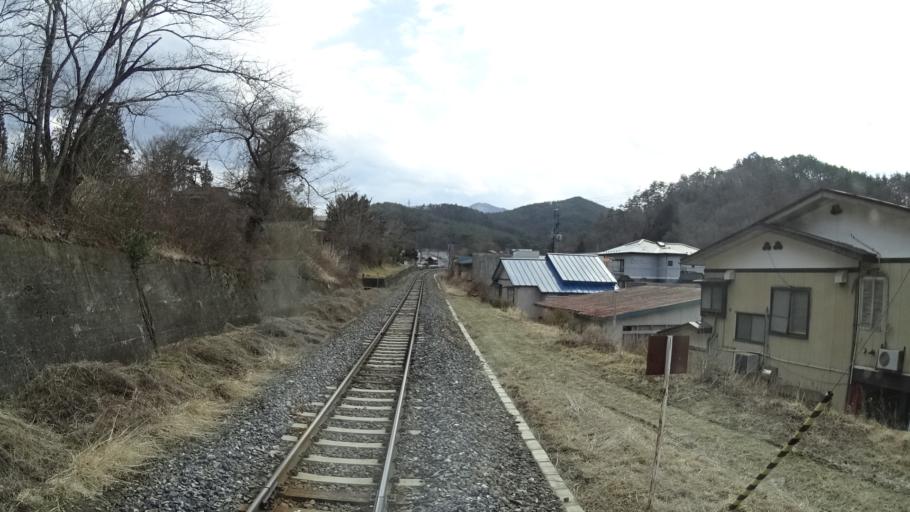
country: JP
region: Iwate
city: Tono
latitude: 39.3495
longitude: 141.3504
